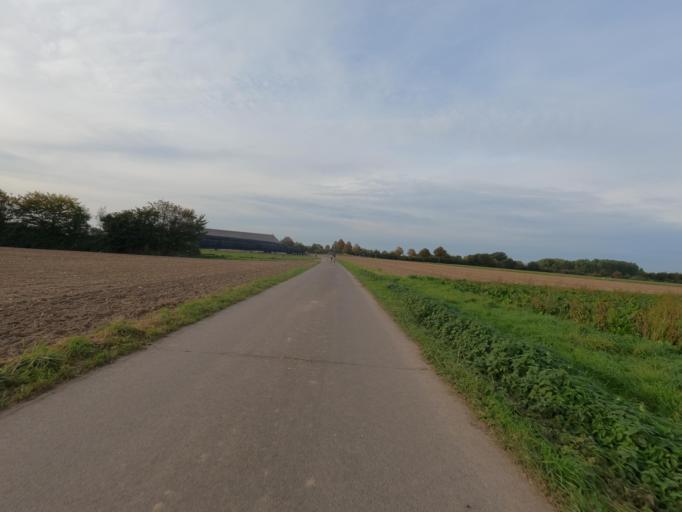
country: DE
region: North Rhine-Westphalia
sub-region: Regierungsbezirk Koln
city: Wassenberg
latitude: 51.0366
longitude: 6.1597
